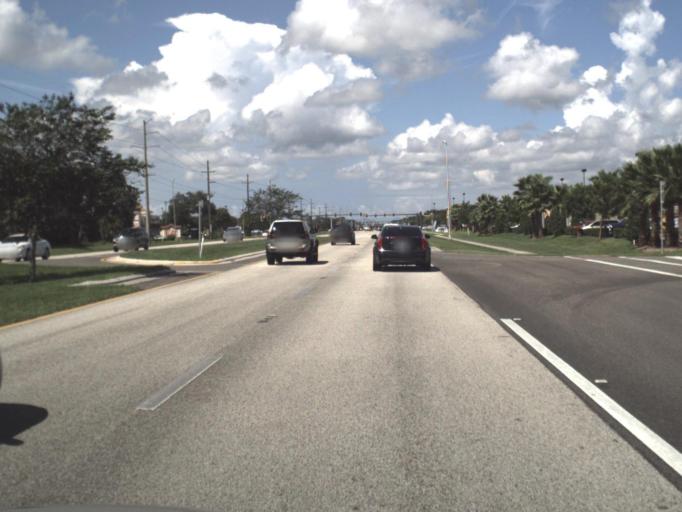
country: US
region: Florida
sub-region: Sarasota County
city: North Port
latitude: 27.0350
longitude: -82.2102
